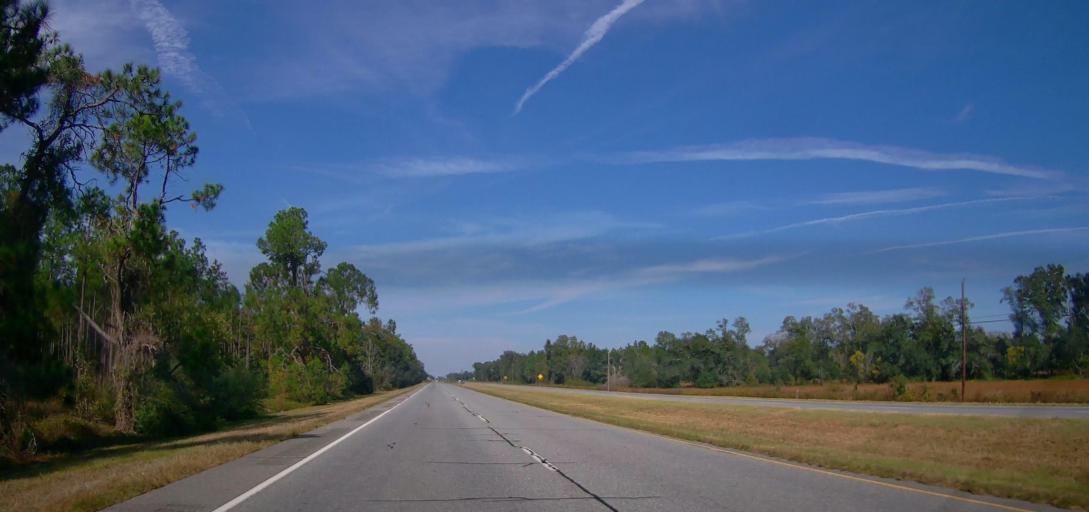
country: US
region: Georgia
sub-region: Dougherty County
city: Putney
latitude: 31.3655
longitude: -84.1542
